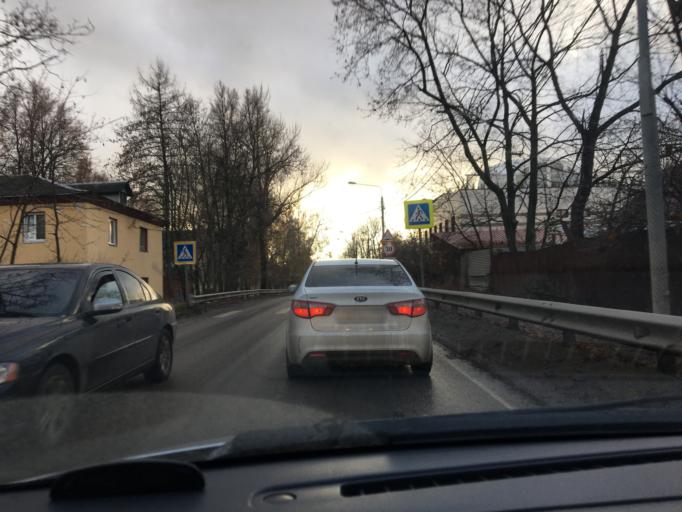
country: RU
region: Moscow
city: Zagor'ye
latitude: 55.5619
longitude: 37.6853
